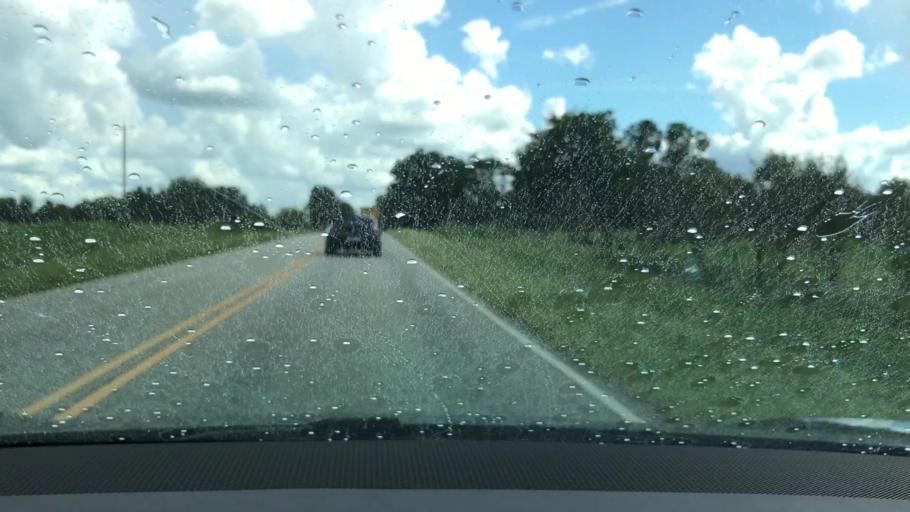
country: US
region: Alabama
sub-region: Montgomery County
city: Pike Road
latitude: 32.2453
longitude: -86.0933
